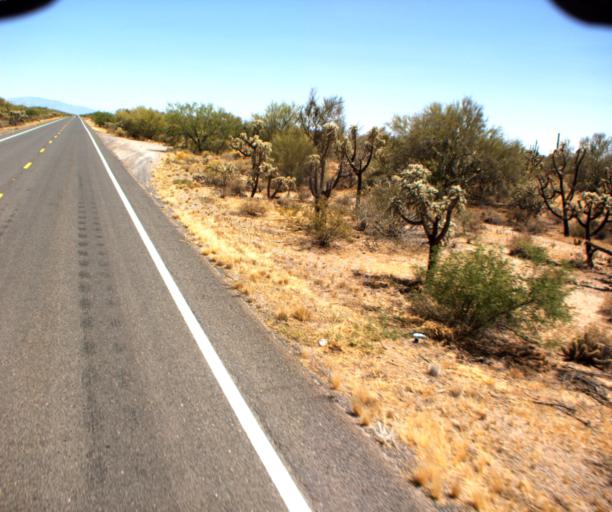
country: US
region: Arizona
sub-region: Pinal County
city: Florence
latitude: 32.8303
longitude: -111.2115
